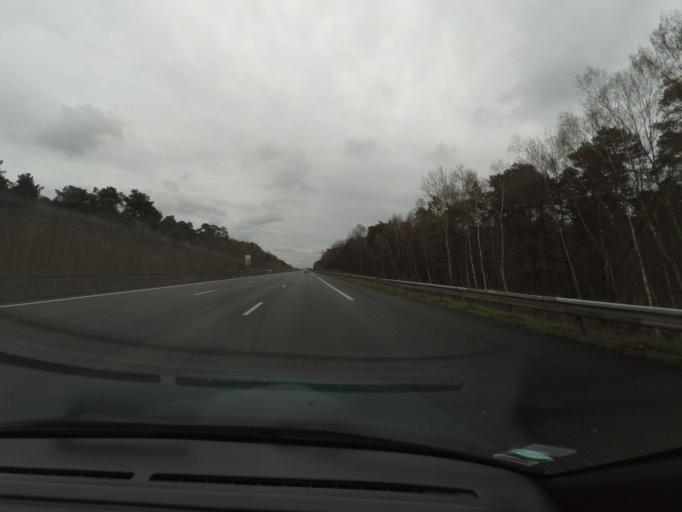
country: FR
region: Pays de la Loire
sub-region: Departement de la Sarthe
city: Montfort-le-Gesnois
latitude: 48.0636
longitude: 0.4025
